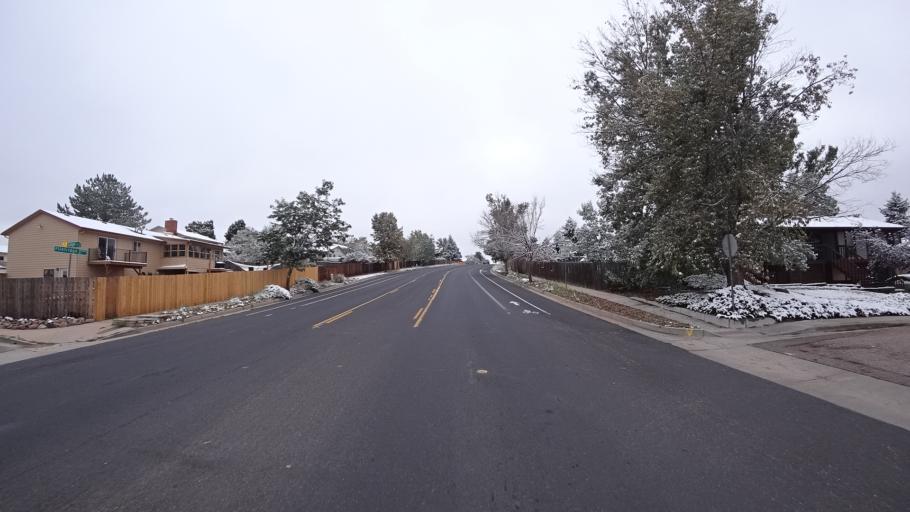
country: US
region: Colorado
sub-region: El Paso County
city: Cimarron Hills
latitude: 38.9234
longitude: -104.7672
